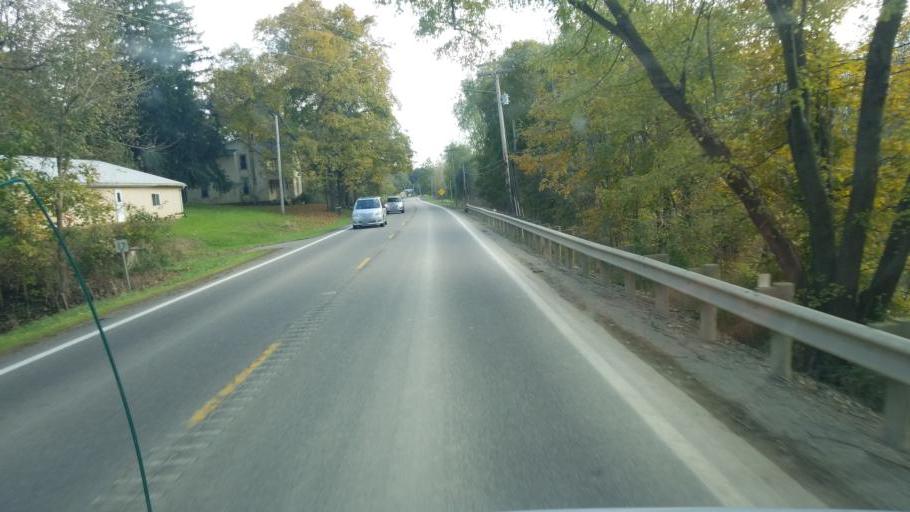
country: US
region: Ohio
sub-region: Wayne County
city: Shreve
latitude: 40.6570
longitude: -81.9414
